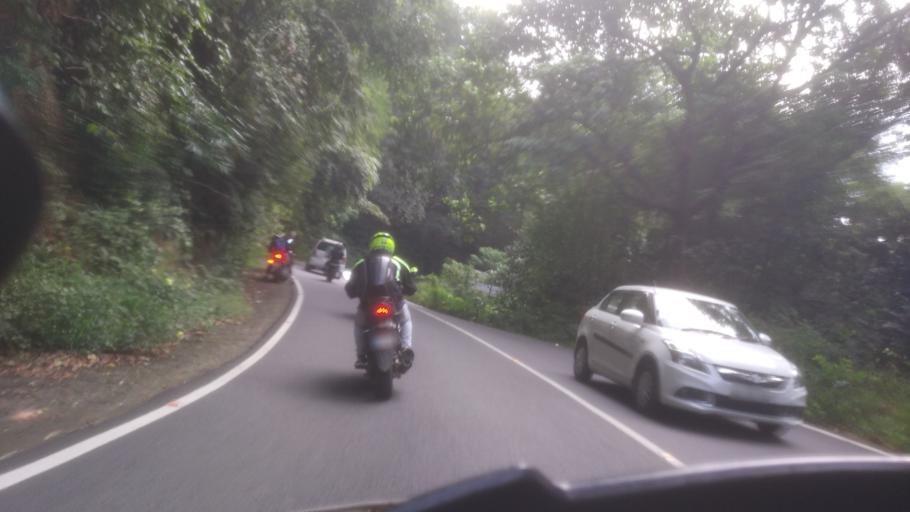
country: IN
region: Kerala
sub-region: Idukki
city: Kuttampuzha
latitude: 10.0656
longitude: 76.7852
